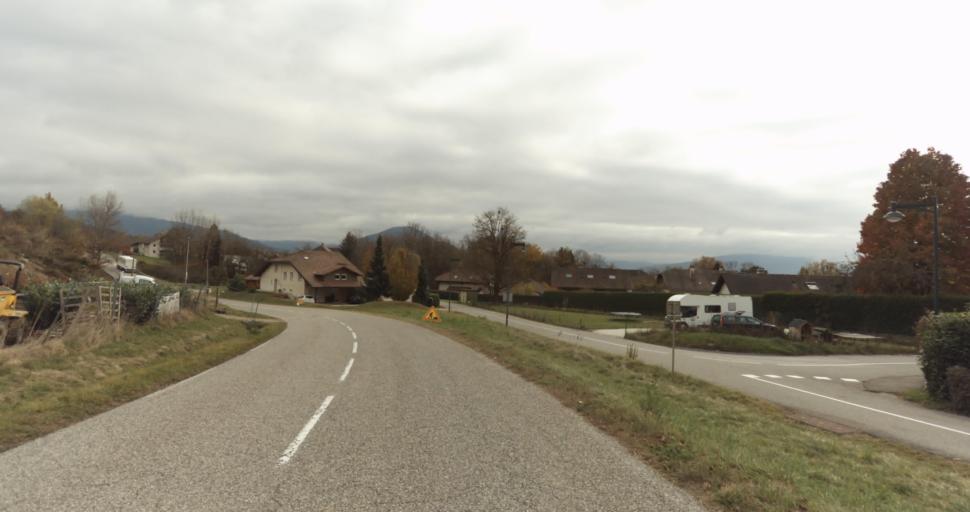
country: FR
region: Rhone-Alpes
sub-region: Departement de la Haute-Savoie
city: Pringy
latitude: 45.9558
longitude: 6.1087
